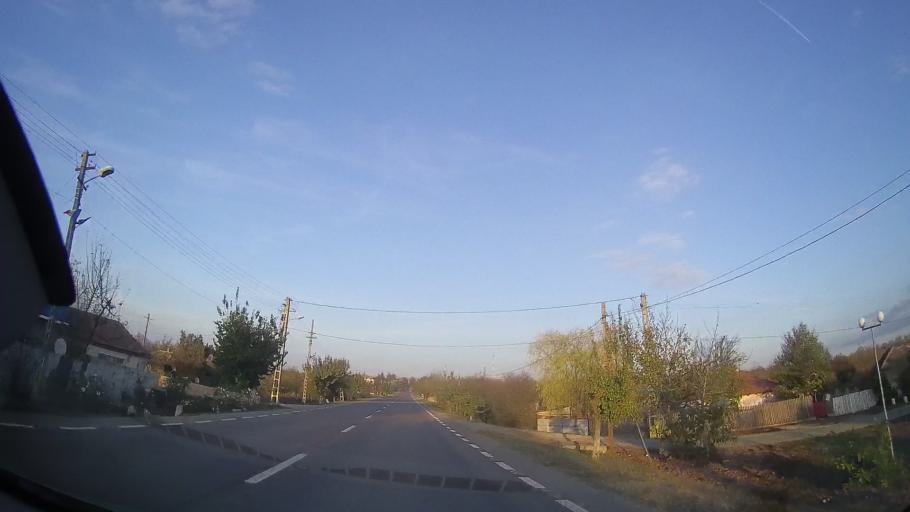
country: RO
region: Constanta
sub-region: Comuna Comana
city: Comana
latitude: 43.8929
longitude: 28.3143
